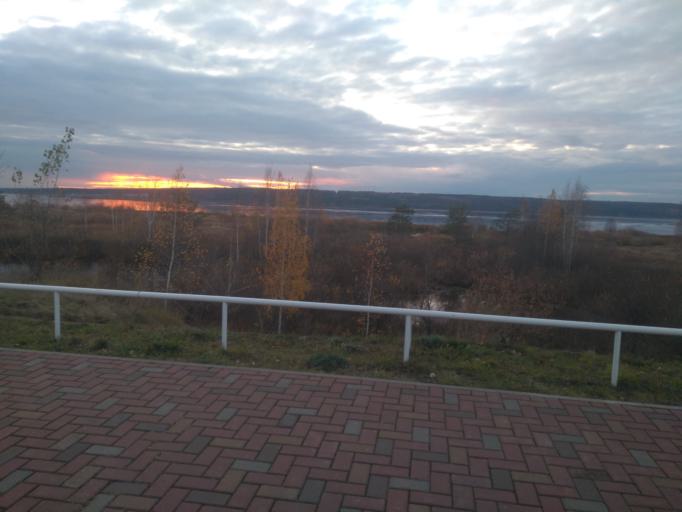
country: RU
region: Tatarstan
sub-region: Tukayevskiy Rayon
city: Naberezhnyye Chelny
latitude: 55.7608
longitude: 52.3716
